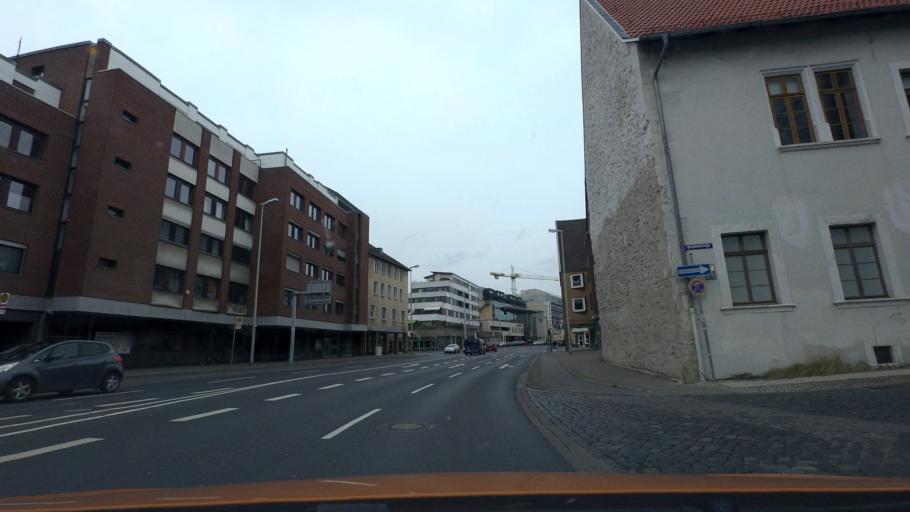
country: DE
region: Lower Saxony
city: Braunschweig
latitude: 52.2619
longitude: 10.5145
